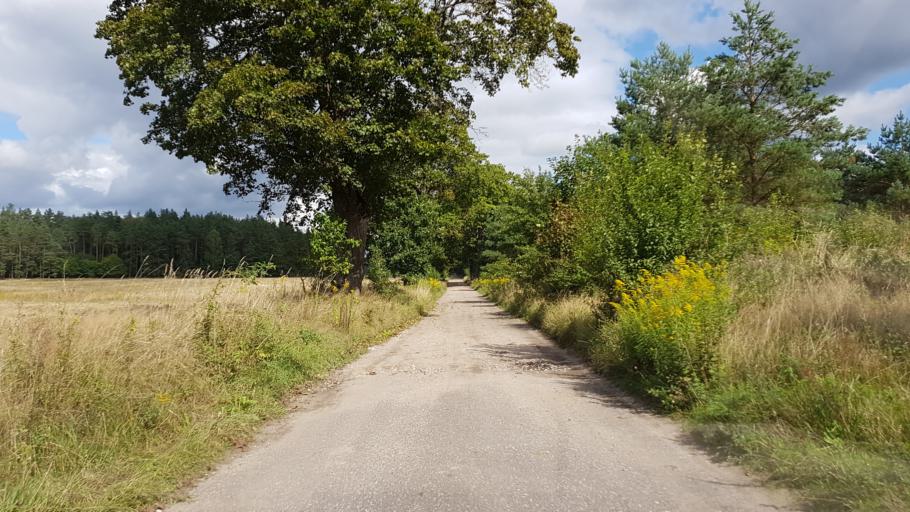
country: PL
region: West Pomeranian Voivodeship
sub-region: Powiat bialogardzki
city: Tychowo
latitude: 53.9961
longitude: 16.3090
